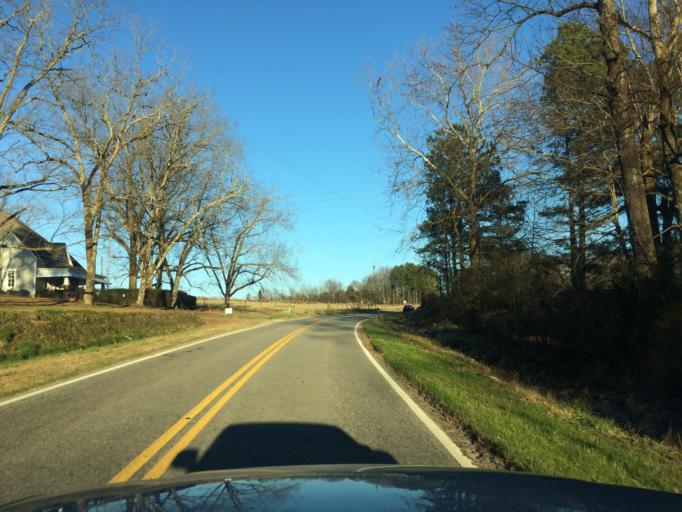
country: US
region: Georgia
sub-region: Barrow County
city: Winder
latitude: 33.9856
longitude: -83.7551
